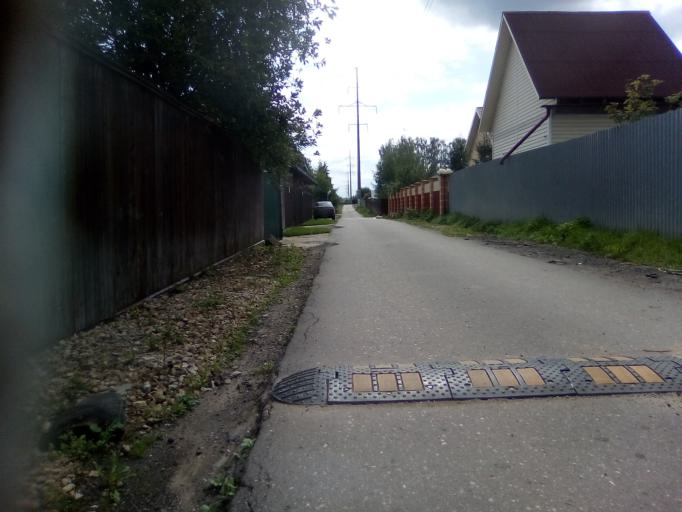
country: RU
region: Moskovskaya
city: Zhavoronki
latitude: 55.6675
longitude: 37.1417
